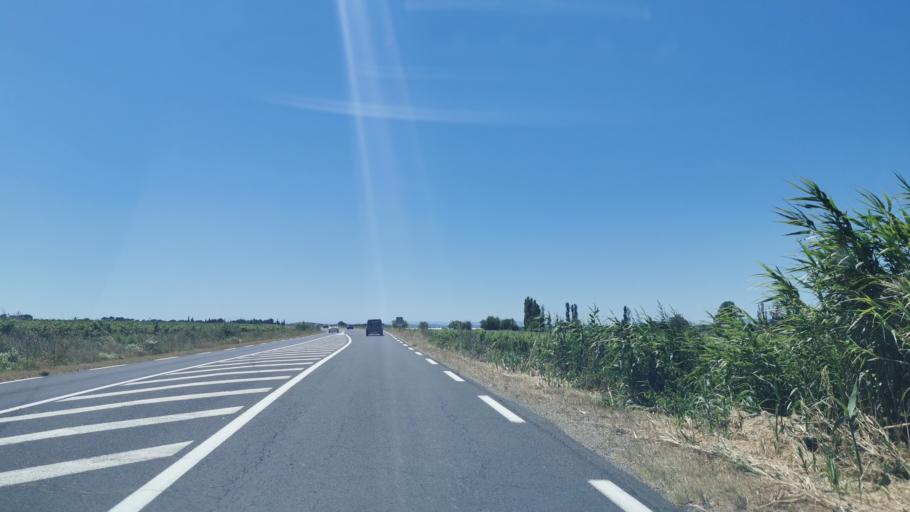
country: FR
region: Languedoc-Roussillon
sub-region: Departement de l'Herault
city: Colombiers
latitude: 43.3044
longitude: 3.1593
